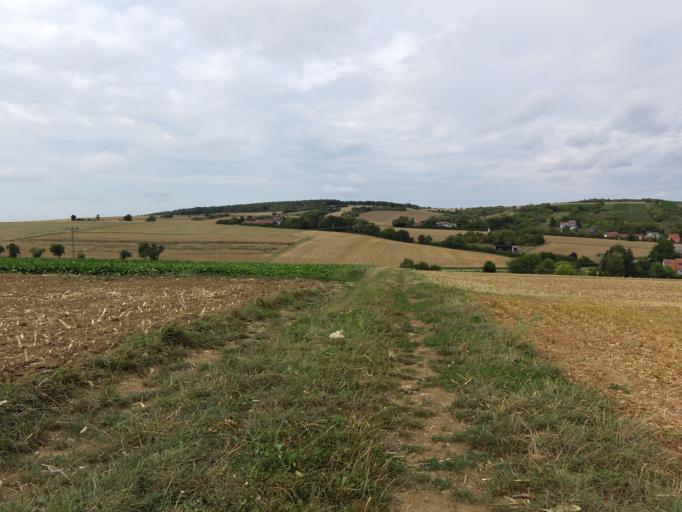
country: DE
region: Bavaria
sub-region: Regierungsbezirk Unterfranken
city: Rimpar
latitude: 49.8548
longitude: 9.9443
